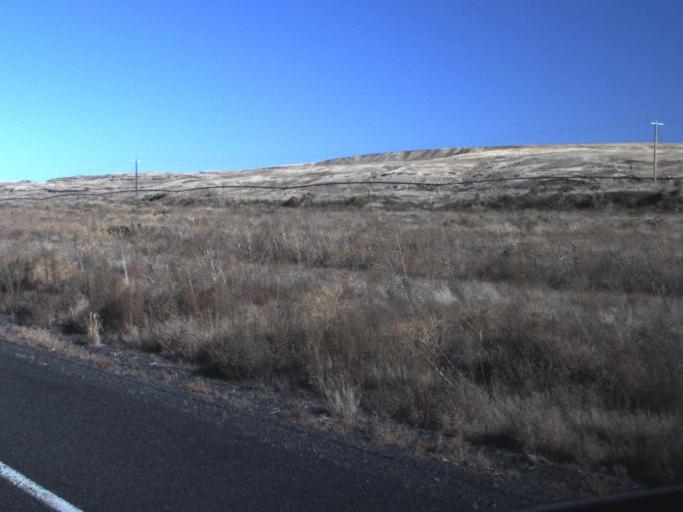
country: US
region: Washington
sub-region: Franklin County
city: Connell
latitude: 46.6848
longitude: -118.4407
